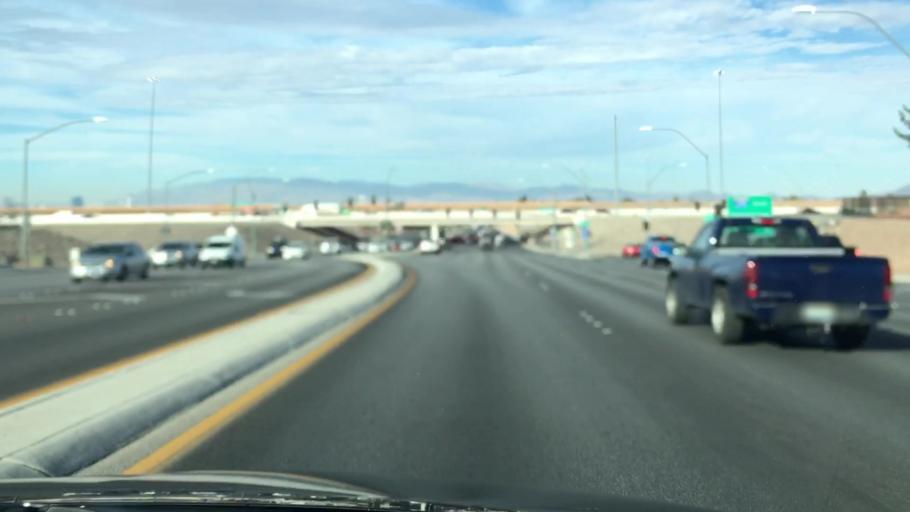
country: US
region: Nevada
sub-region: Clark County
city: Whitney
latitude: 36.0214
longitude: -115.1005
